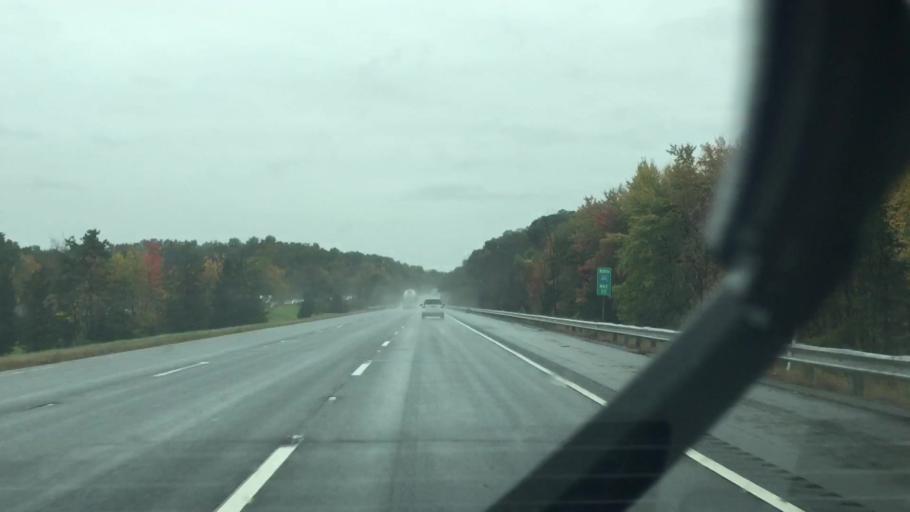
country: US
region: Massachusetts
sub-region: Essex County
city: Merrimac
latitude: 42.8123
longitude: -71.0261
